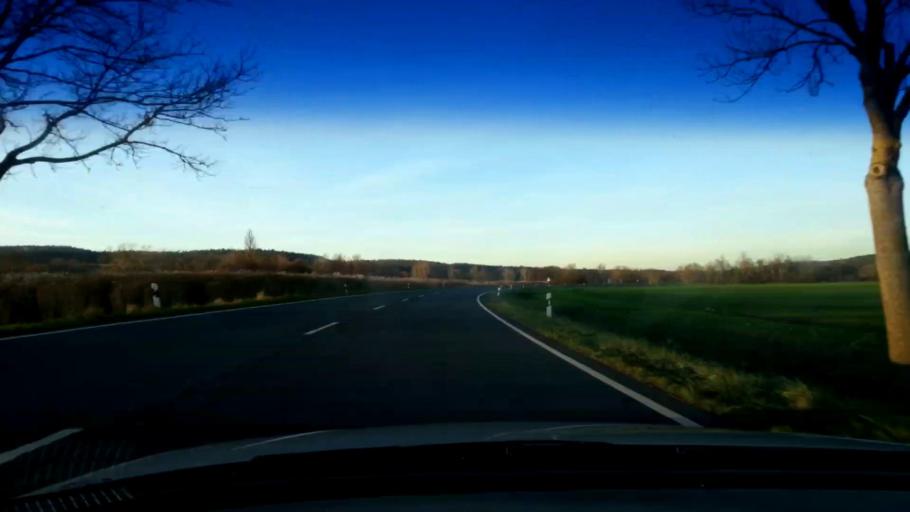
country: DE
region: Bavaria
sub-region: Upper Franconia
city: Rattelsdorf
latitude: 50.0238
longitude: 10.8835
